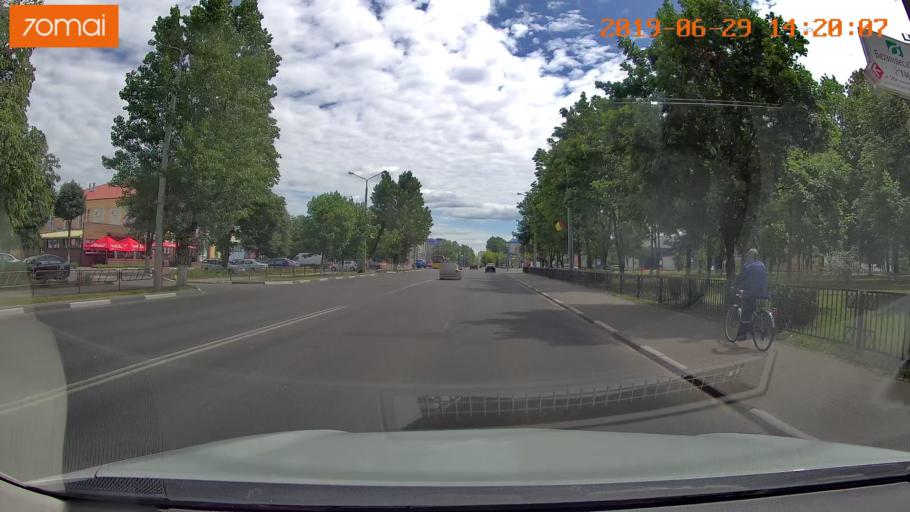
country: BY
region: Minsk
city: Salihorsk
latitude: 52.7942
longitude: 27.5417
